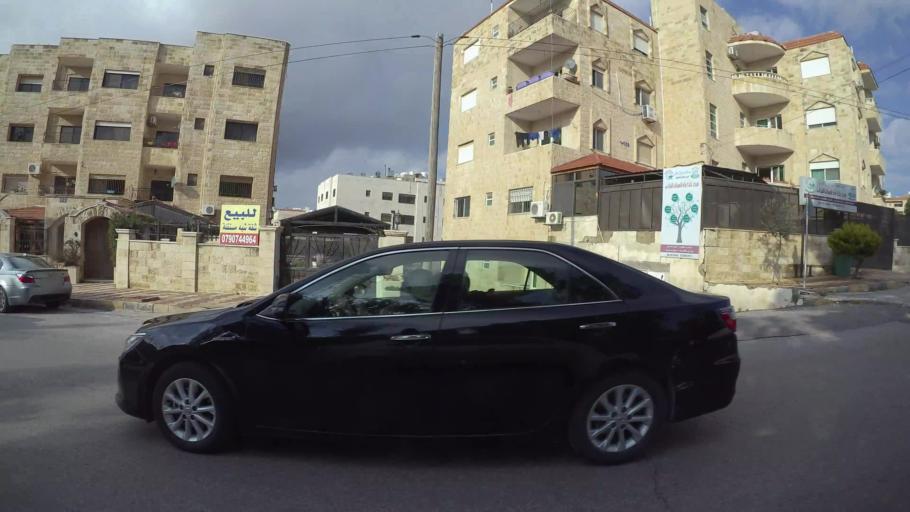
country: JO
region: Amman
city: Wadi as Sir
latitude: 31.9822
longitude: 35.8420
